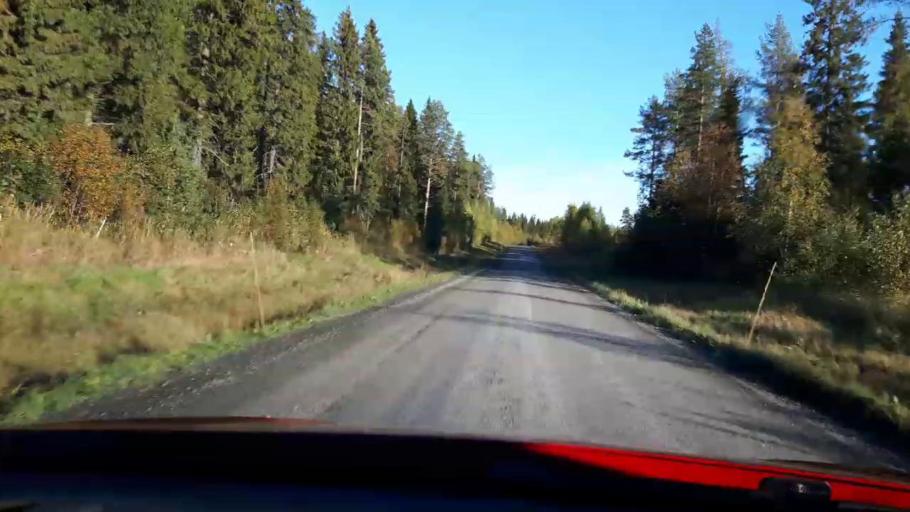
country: SE
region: Jaemtland
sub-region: OEstersunds Kommun
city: Lit
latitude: 63.6699
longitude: 14.6990
